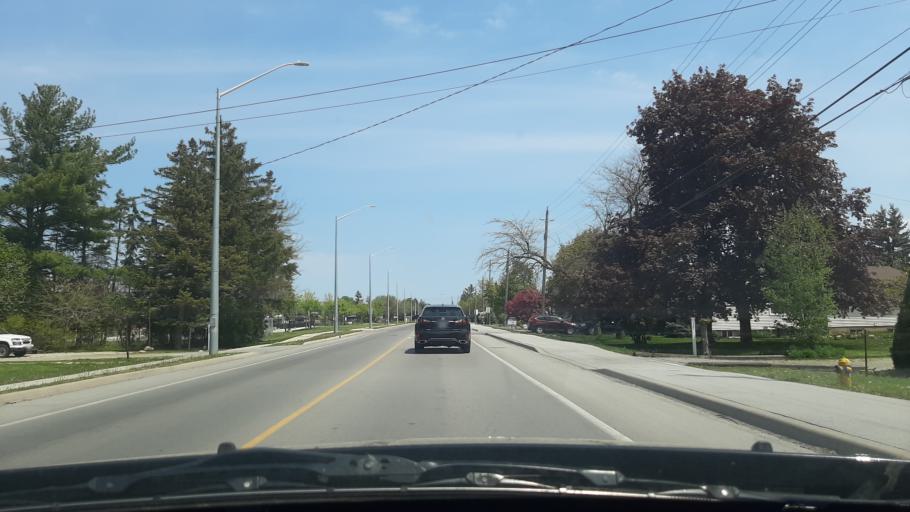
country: US
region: New York
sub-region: Niagara County
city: Youngstown
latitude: 43.2150
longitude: -79.1312
